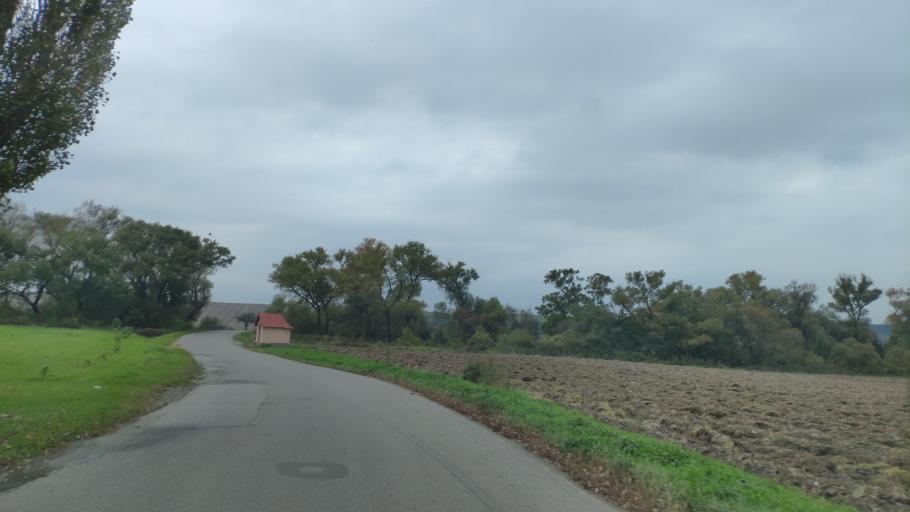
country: SK
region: Kosicky
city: Kosice
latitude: 48.6381
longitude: 21.3776
